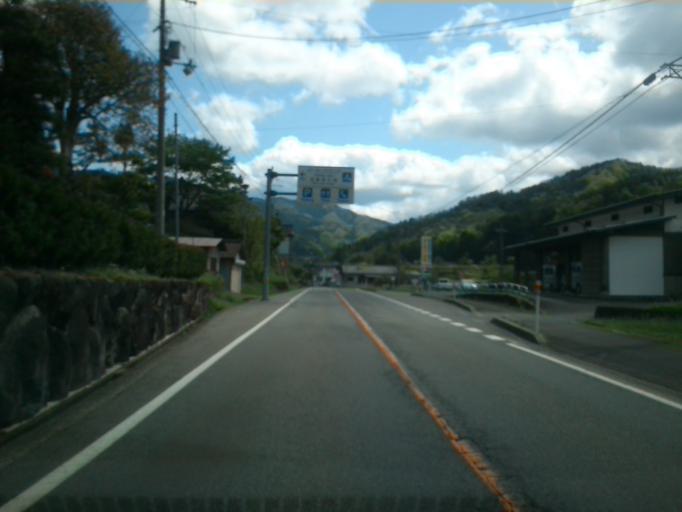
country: JP
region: Kyoto
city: Fukuchiyama
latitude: 35.4226
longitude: 135.0077
